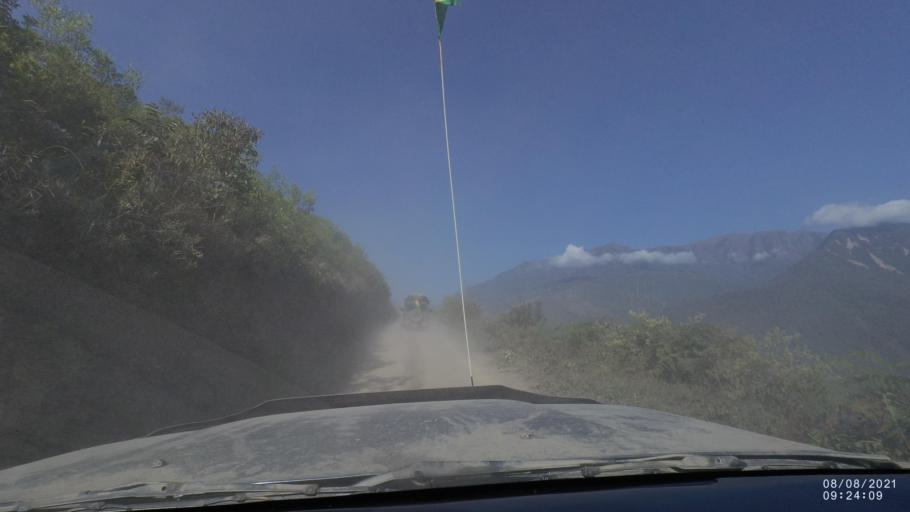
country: BO
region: La Paz
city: Quime
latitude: -16.5770
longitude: -66.7208
